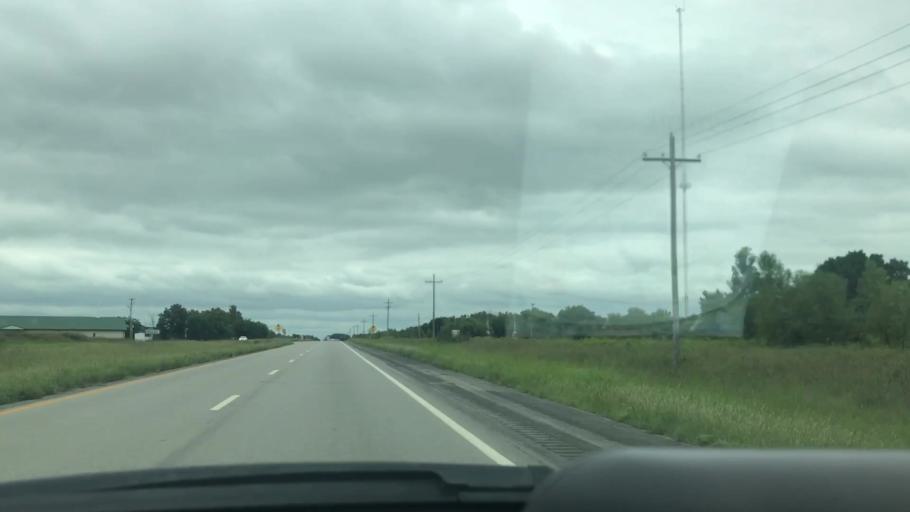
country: US
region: Oklahoma
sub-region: Mayes County
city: Pryor
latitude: 36.4216
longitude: -95.2772
